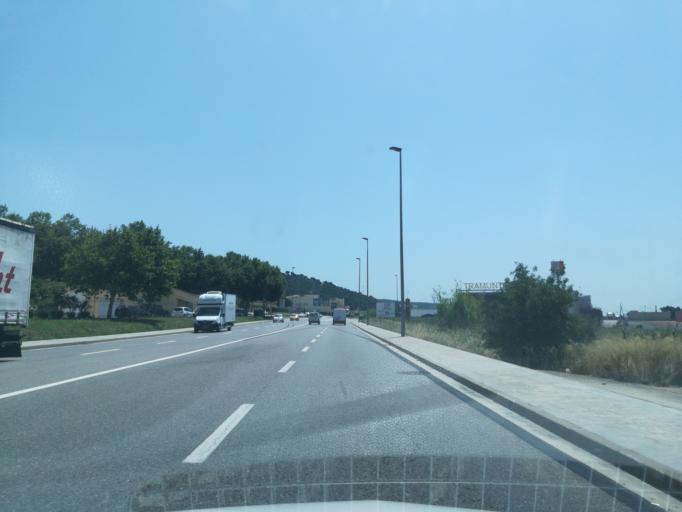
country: ES
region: Catalonia
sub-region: Provincia de Girona
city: la Jonquera
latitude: 42.4127
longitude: 2.8747
